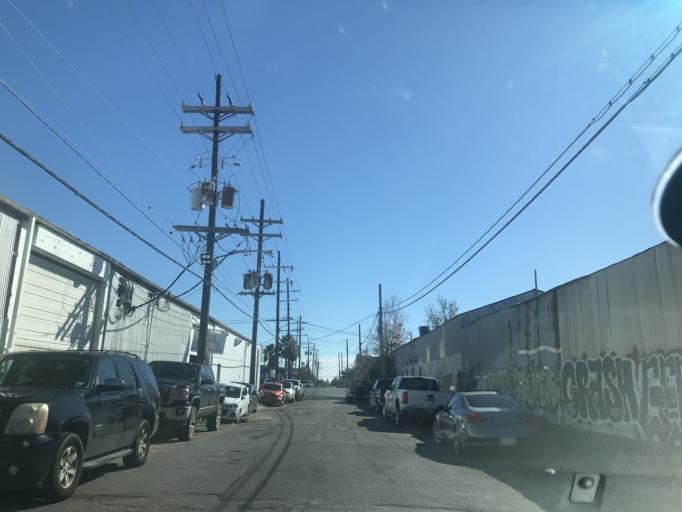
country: US
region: Louisiana
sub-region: Orleans Parish
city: New Orleans
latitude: 29.9532
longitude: -90.0988
